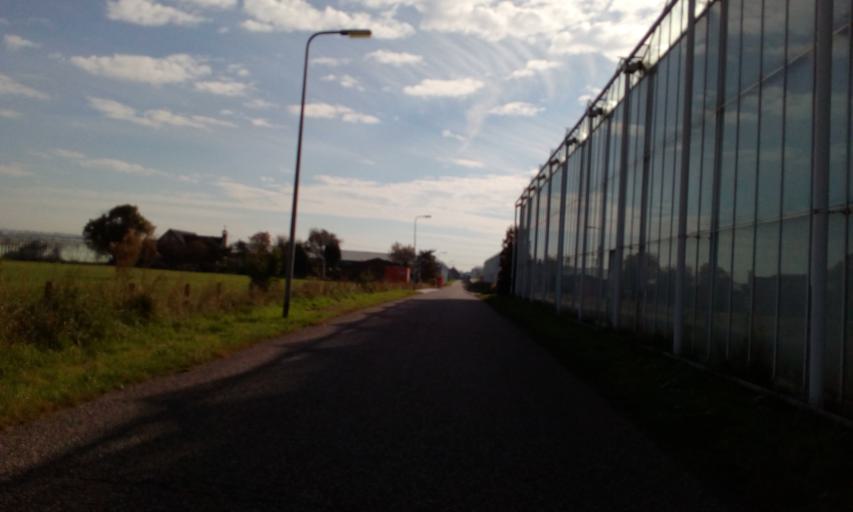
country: NL
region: South Holland
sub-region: Gemeente Westland
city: Kwintsheul
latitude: 52.0085
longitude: 4.2634
